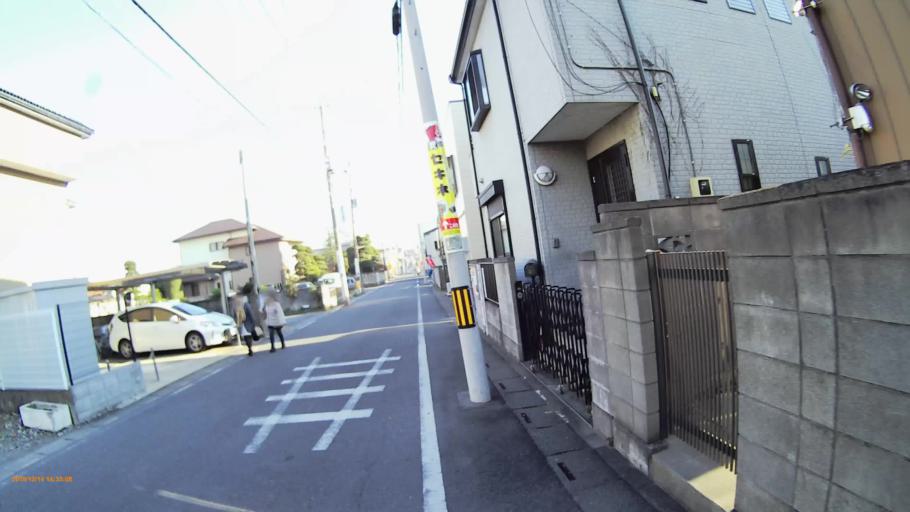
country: JP
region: Saitama
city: Konosu
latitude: 36.0348
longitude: 139.5323
